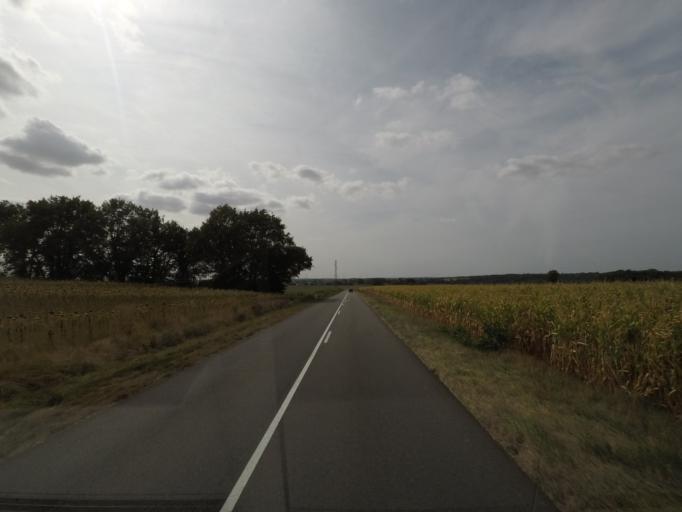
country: FR
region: Poitou-Charentes
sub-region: Departement de la Charente
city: Ruffec
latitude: 46.0250
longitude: 0.2433
